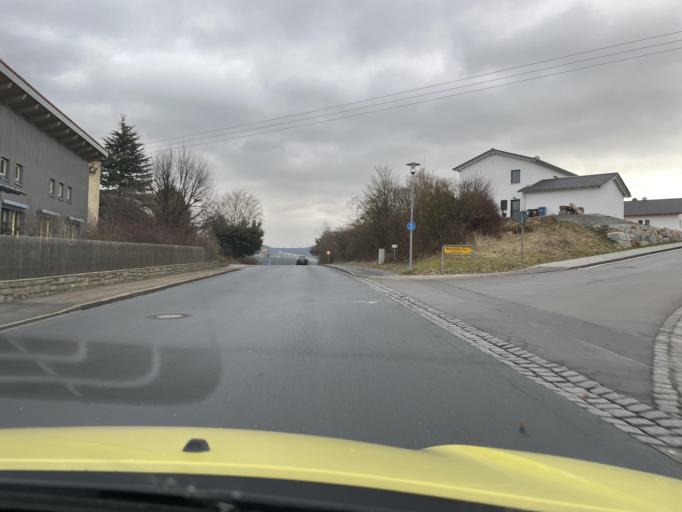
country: DE
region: Bavaria
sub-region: Upper Palatinate
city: Traitsching
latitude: 49.1750
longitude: 12.6820
